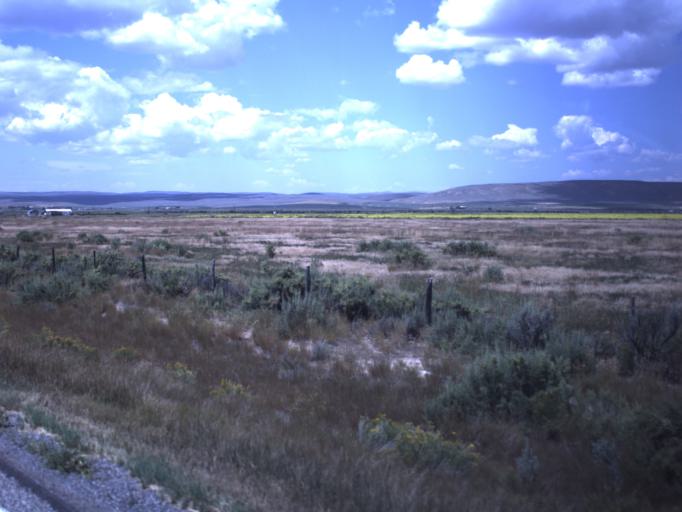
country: US
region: Utah
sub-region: Rich County
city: Randolph
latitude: 41.7788
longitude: -111.0548
